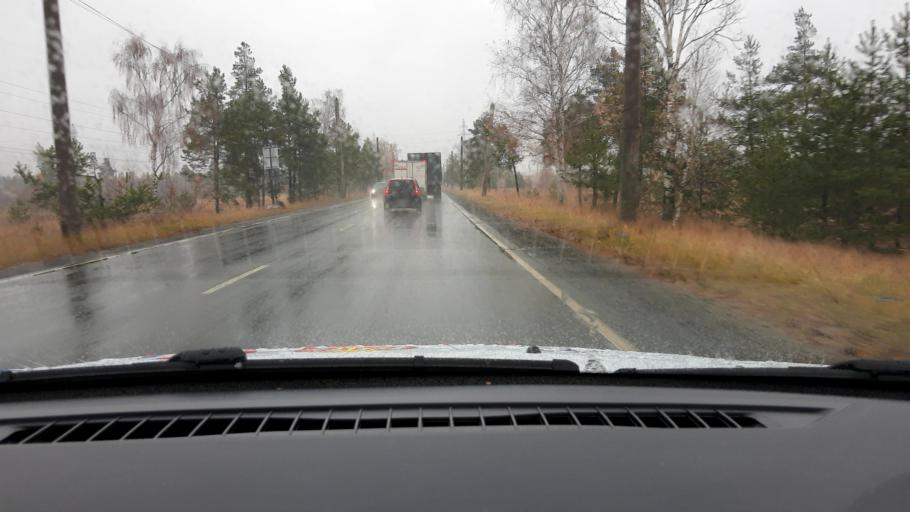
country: RU
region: Nizjnij Novgorod
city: Babino
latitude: 56.2822
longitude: 43.5742
